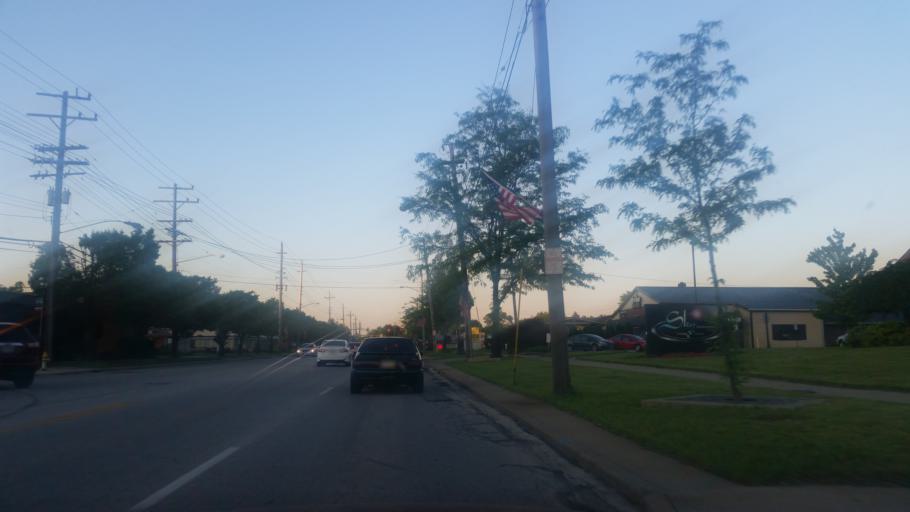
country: US
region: Ohio
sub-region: Cuyahoga County
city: Parma Heights
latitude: 41.3865
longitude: -81.7680
